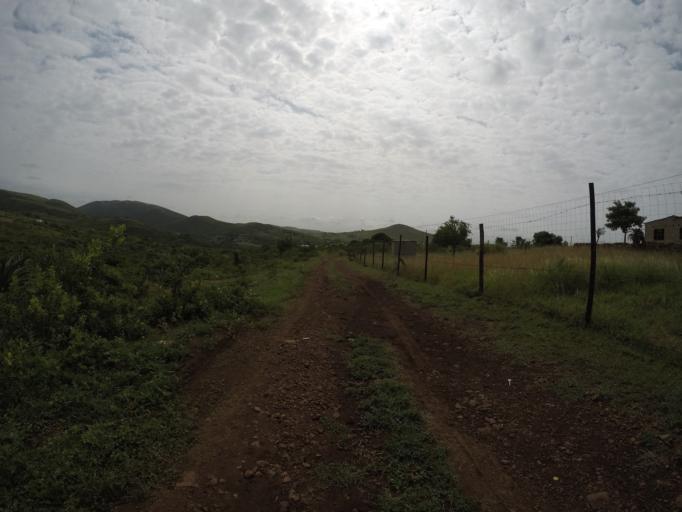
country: ZA
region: KwaZulu-Natal
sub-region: uThungulu District Municipality
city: Empangeni
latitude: -28.6229
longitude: 31.9077
